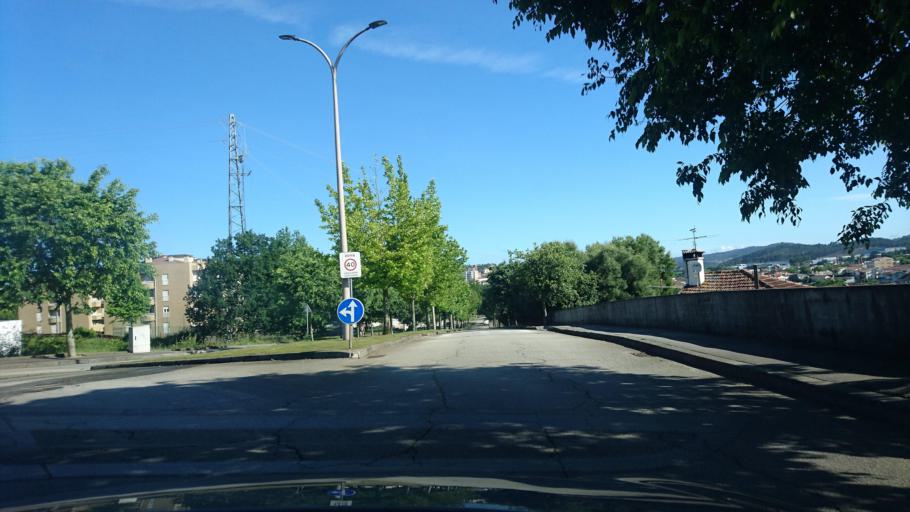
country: PT
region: Aveiro
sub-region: Sao Joao da Madeira
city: Sao Joao da Madeira
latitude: 40.8897
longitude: -8.4842
